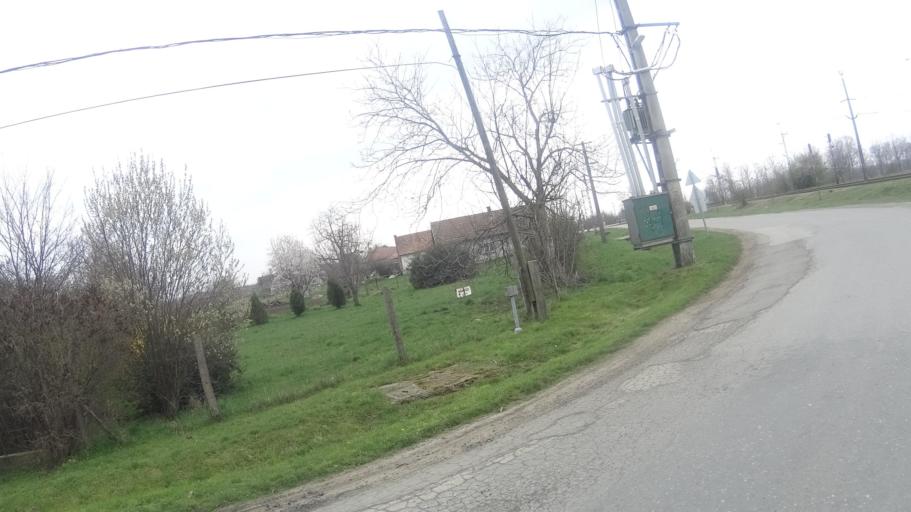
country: HU
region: Fejer
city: Sarosd
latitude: 46.9761
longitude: 18.6351
